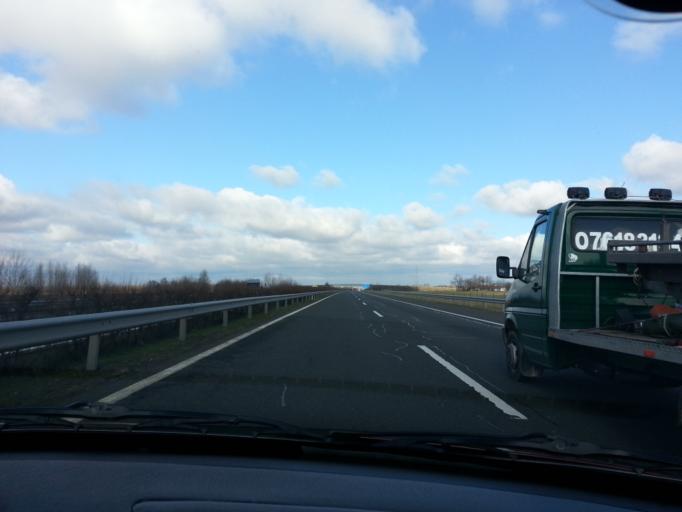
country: HU
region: Csongrad
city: Kistelek
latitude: 46.4493
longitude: 19.9350
